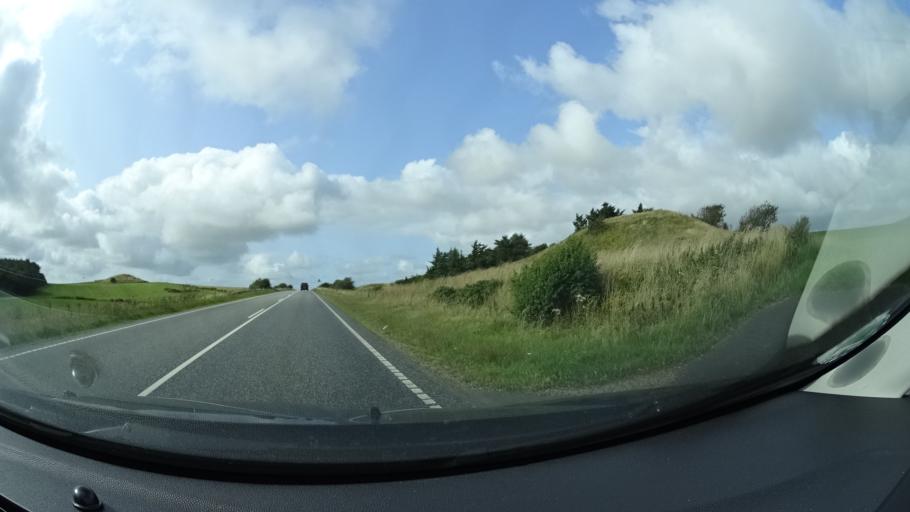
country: DK
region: Central Jutland
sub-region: Lemvig Kommune
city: Harboore
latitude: 56.5796
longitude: 8.2030
